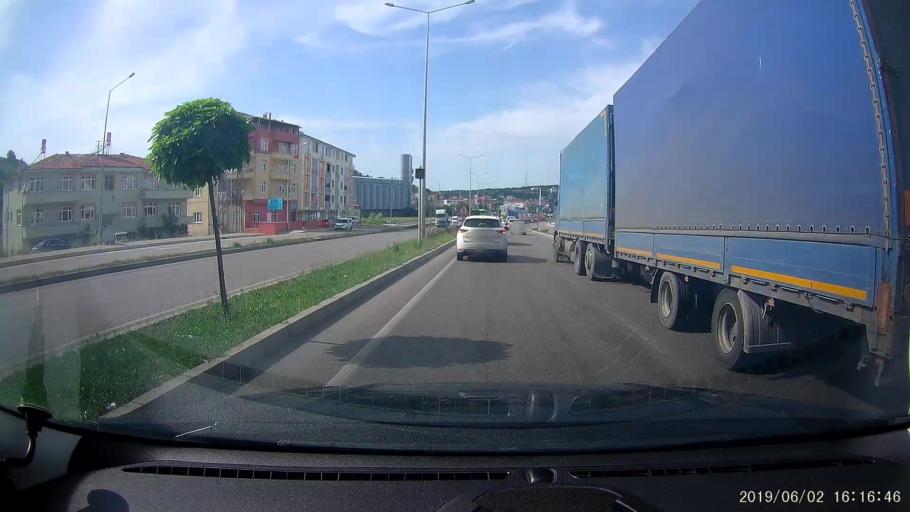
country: TR
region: Samsun
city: Havza
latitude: 40.9585
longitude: 35.6660
